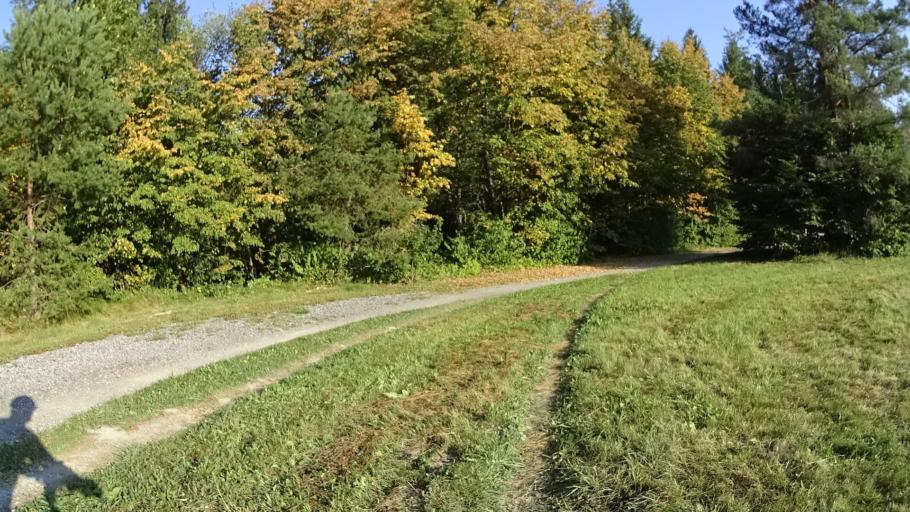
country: AT
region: Carinthia
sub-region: Politischer Bezirk Villach Land
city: Rosegg
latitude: 46.5690
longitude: 14.0261
